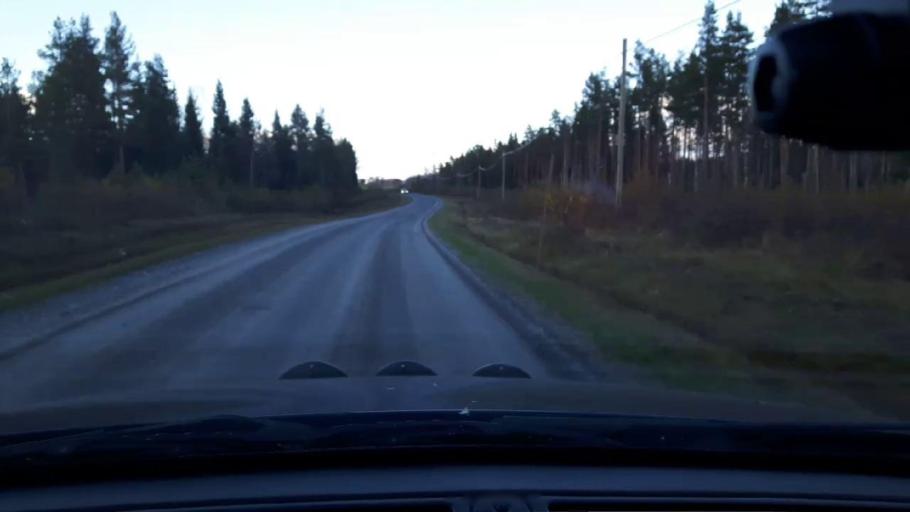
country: SE
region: Jaemtland
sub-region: Krokoms Kommun
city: Krokom
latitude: 63.0715
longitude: 14.2687
